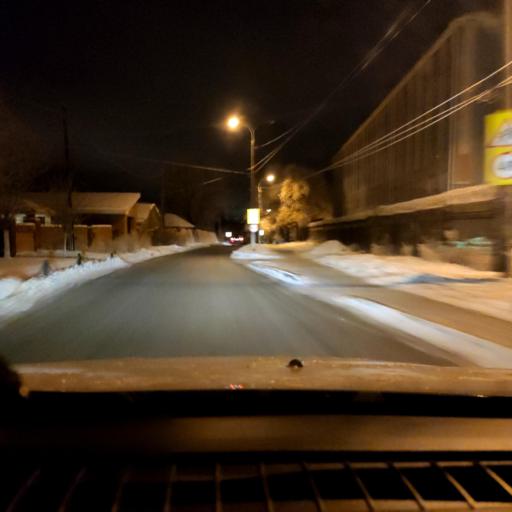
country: RU
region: Samara
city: Novosemeykino
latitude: 53.3445
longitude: 50.2282
